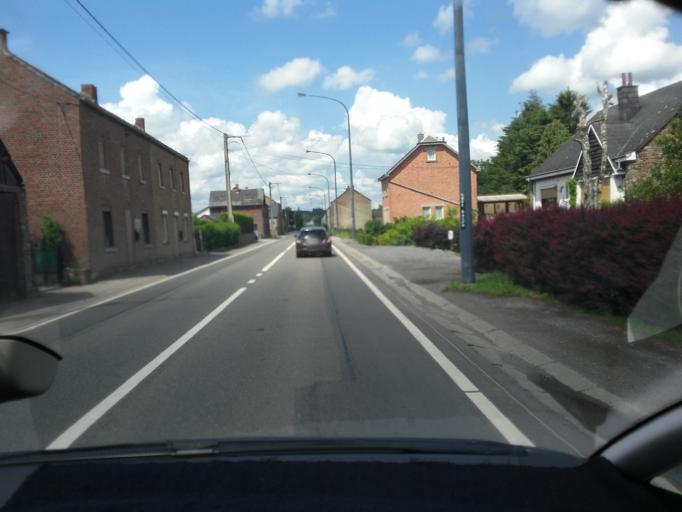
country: BE
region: Wallonia
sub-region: Province de Namur
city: Rochefort
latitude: 50.1686
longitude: 5.2115
